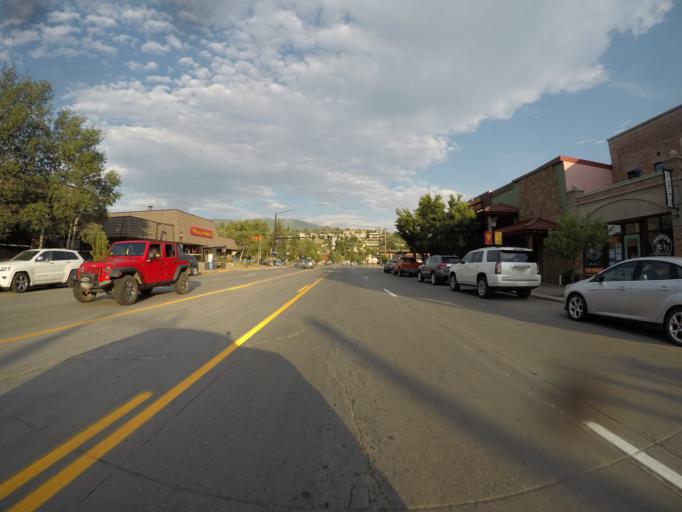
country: US
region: Colorado
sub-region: Routt County
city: Steamboat Springs
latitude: 40.4834
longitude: -106.8300
